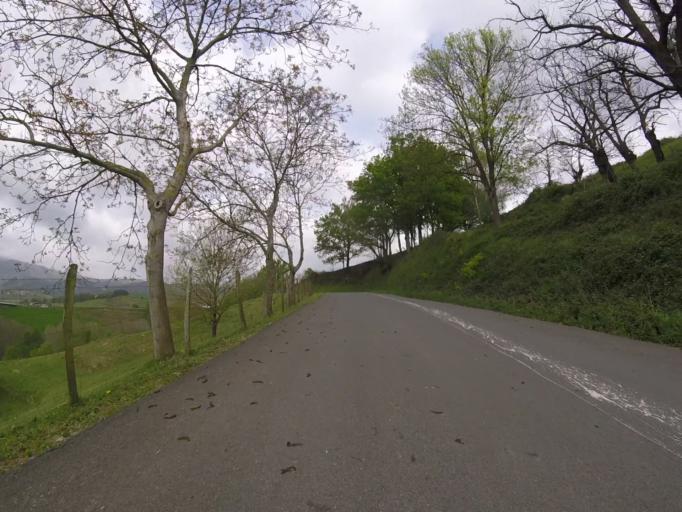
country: ES
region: Basque Country
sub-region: Provincia de Guipuzcoa
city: Zizurkil
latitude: 43.2043
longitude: -2.0762
